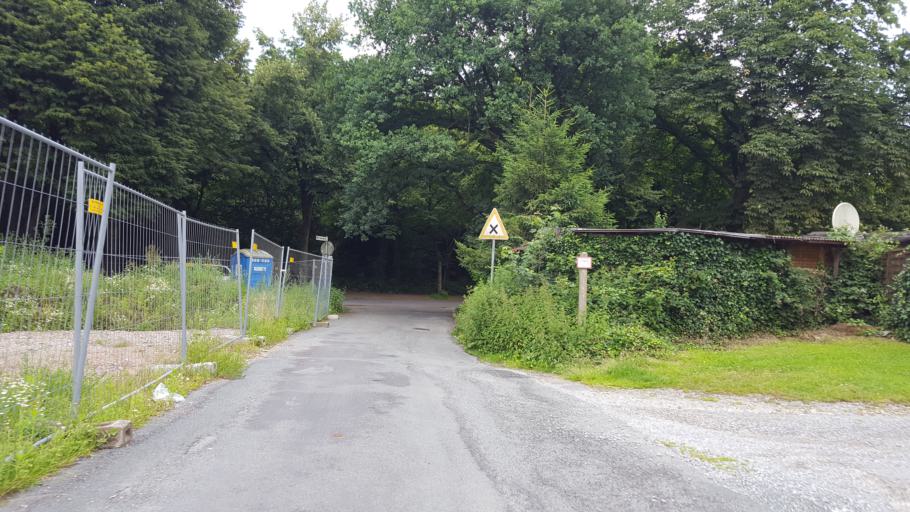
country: DE
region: North Rhine-Westphalia
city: Oer-Erkenschwick
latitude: 51.6440
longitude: 7.2750
